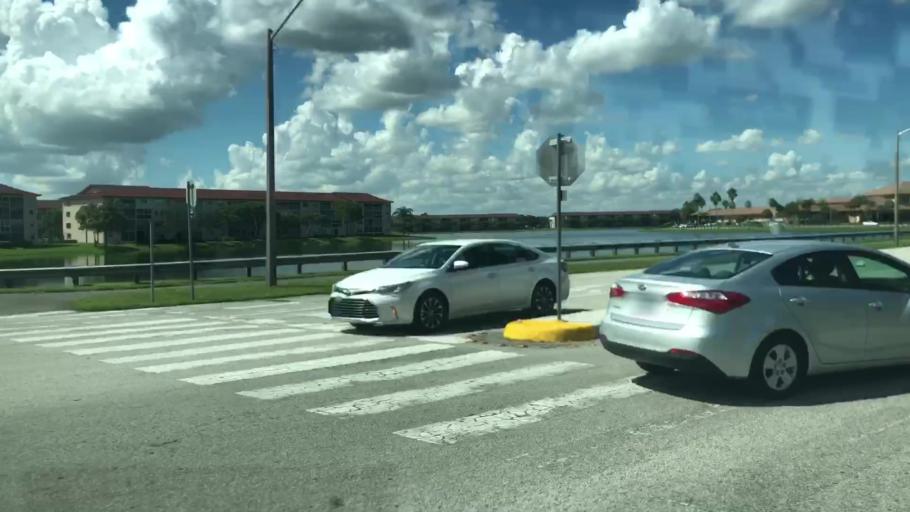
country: US
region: Florida
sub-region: Broward County
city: Sunshine Ranches
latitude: 26.0002
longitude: -80.3219
